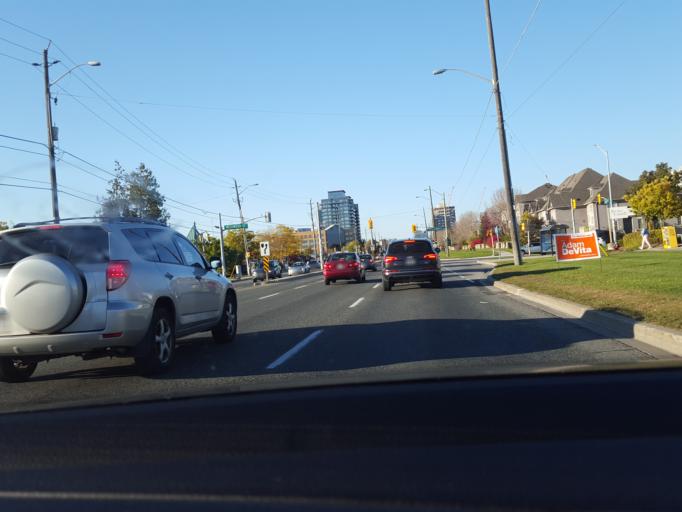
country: CA
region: Ontario
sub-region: York
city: Richmond Hill
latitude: 43.8436
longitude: -79.4307
